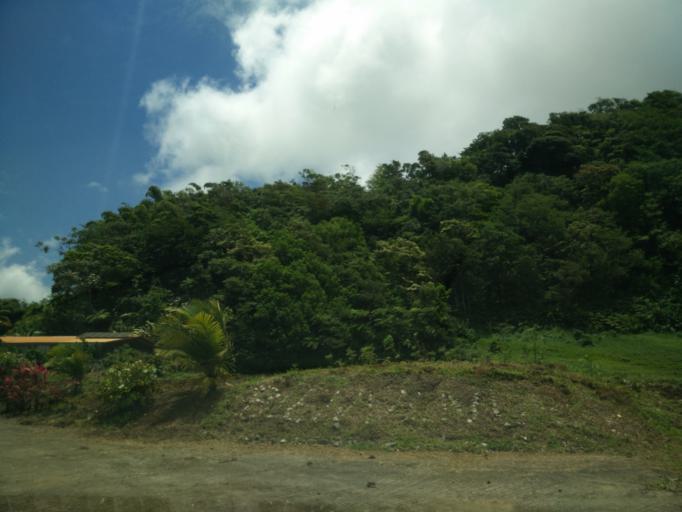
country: MQ
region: Martinique
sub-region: Martinique
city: Le Morne-Rouge
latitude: 14.7846
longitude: -61.1432
